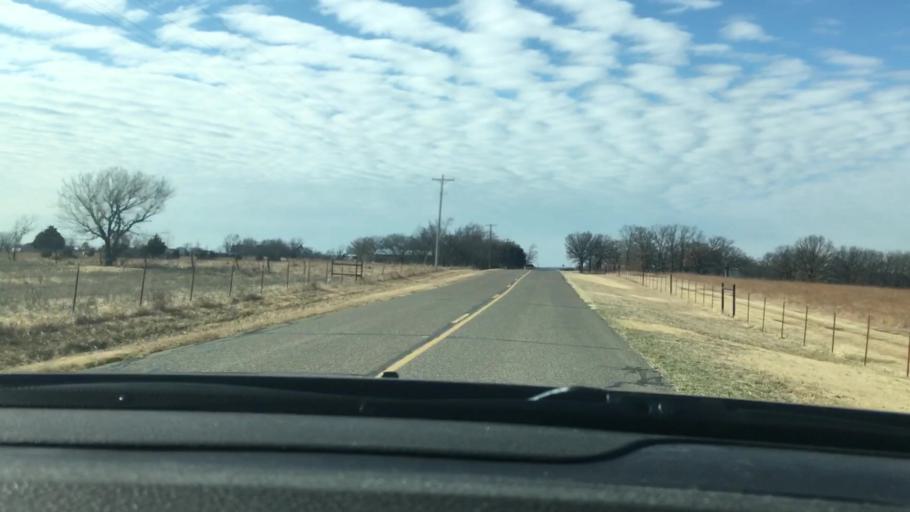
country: US
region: Oklahoma
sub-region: Garvin County
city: Pauls Valley
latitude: 34.7386
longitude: -97.1336
